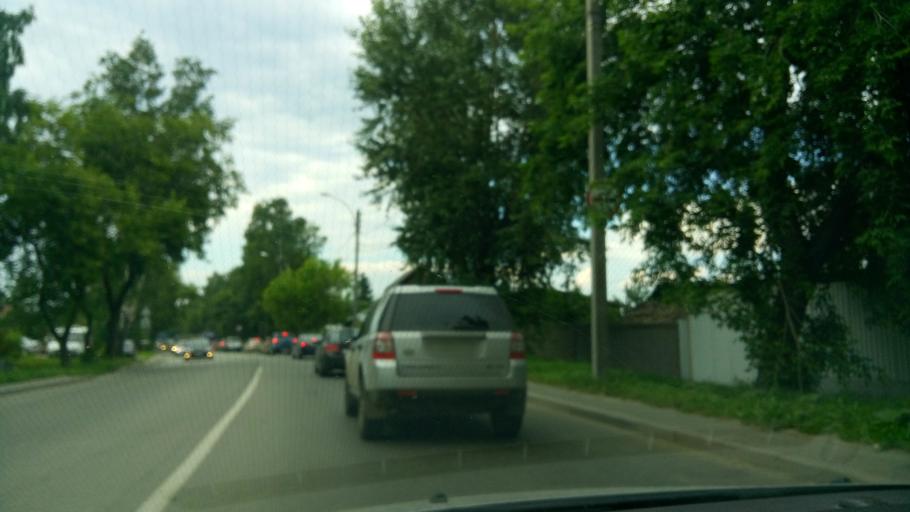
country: RU
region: Sverdlovsk
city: Yekaterinburg
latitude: 56.8777
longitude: 60.6922
